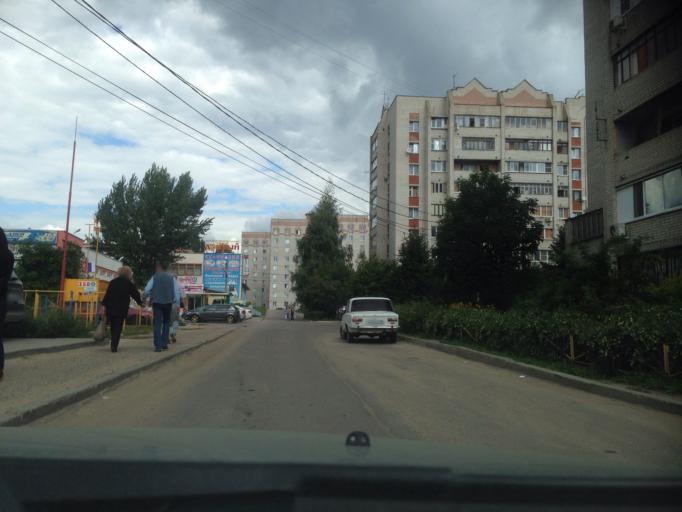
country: RU
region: Voronezj
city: Podgornoye
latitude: 51.7266
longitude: 39.2015
